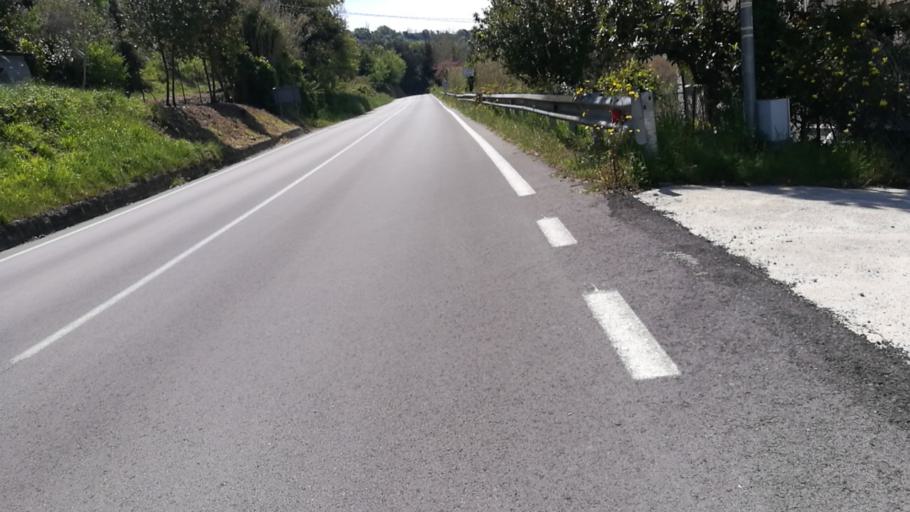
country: IT
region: Abruzzo
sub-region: Provincia di Chieti
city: Marina di San Vito
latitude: 42.3013
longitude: 14.4421
